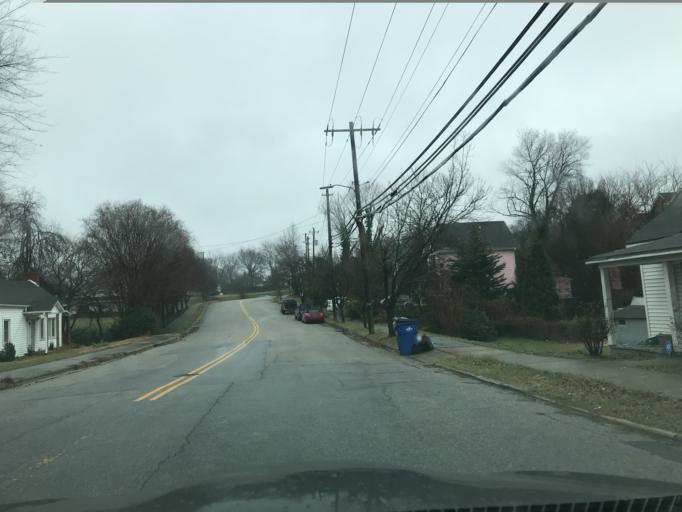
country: US
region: North Carolina
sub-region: Wake County
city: Raleigh
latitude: 35.7705
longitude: -78.6337
